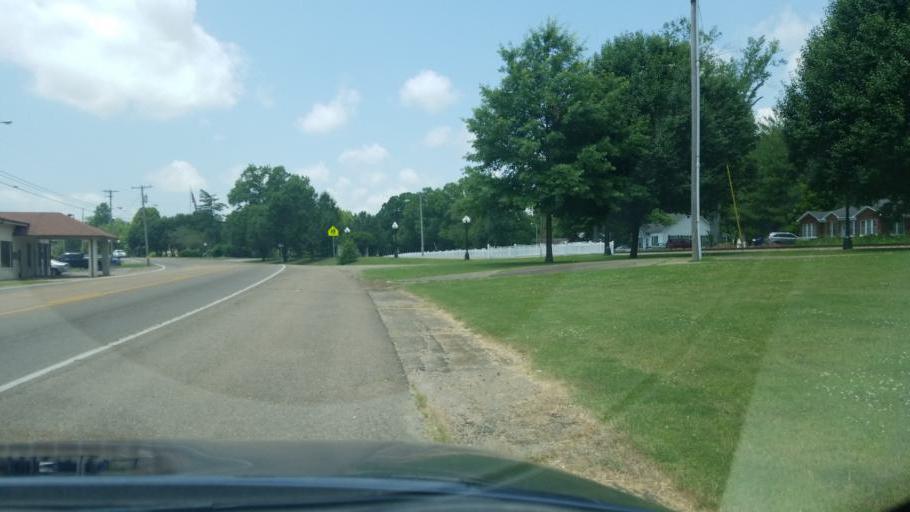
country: US
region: Tennessee
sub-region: Carroll County
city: Huntingdon
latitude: 36.0040
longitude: -88.4176
